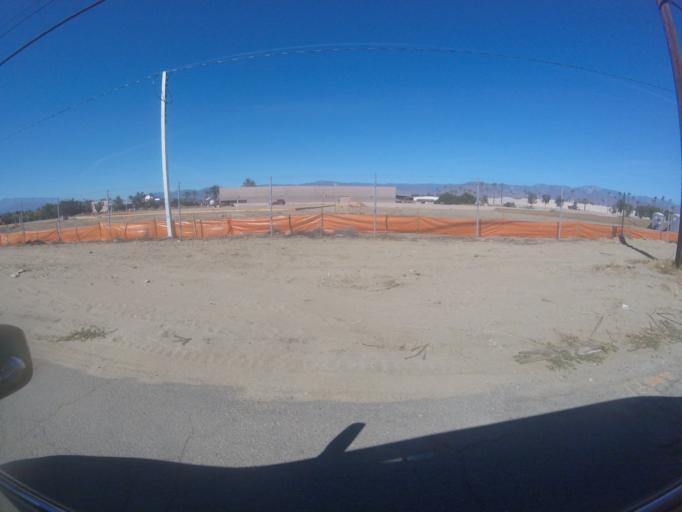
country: US
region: California
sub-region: San Bernardino County
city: Redlands
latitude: 34.0592
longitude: -117.2123
